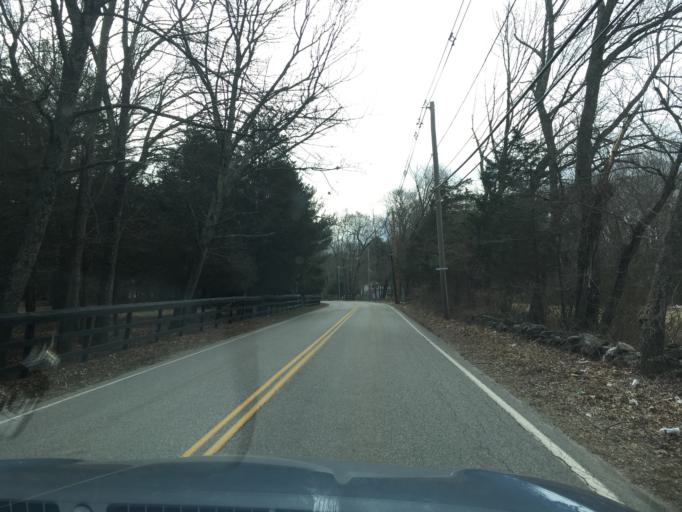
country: US
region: Rhode Island
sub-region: Kent County
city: East Greenwich
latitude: 41.6437
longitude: -71.4503
